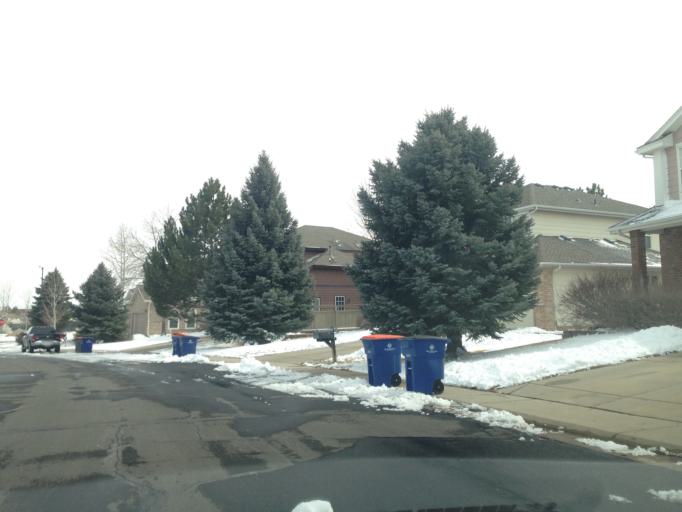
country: US
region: Colorado
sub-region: Boulder County
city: Lafayette
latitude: 39.9711
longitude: -105.0962
